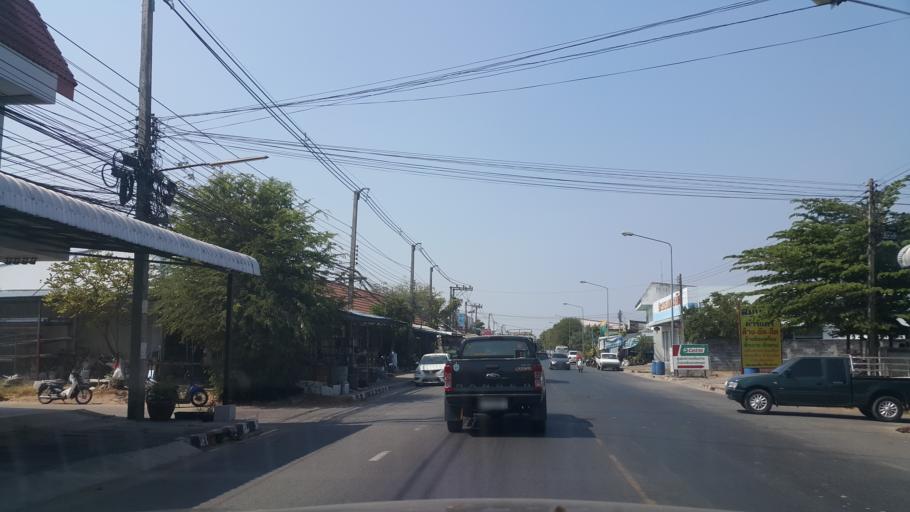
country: TH
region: Buriram
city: Satuek
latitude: 15.2940
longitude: 103.2868
